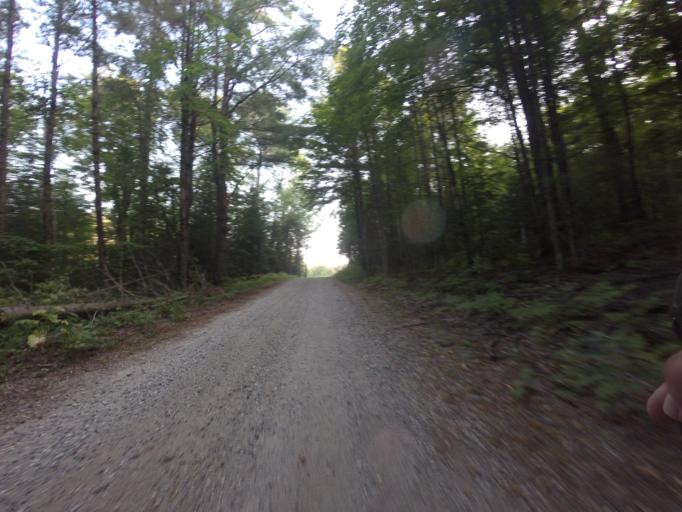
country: CA
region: Ontario
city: Renfrew
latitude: 45.0765
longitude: -76.7221
